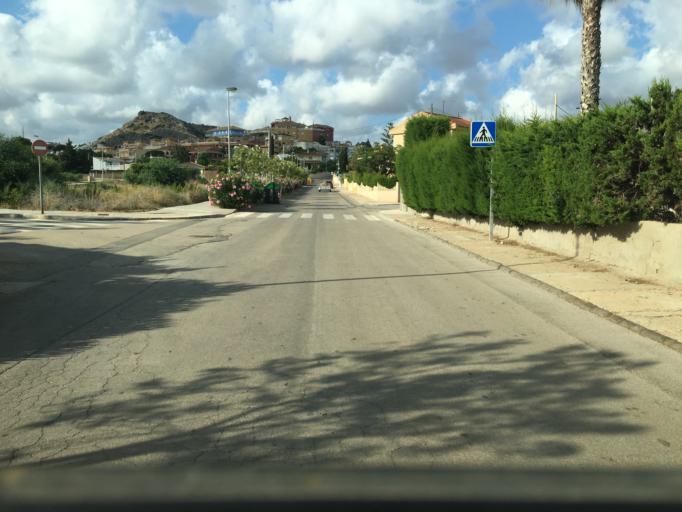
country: ES
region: Murcia
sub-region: Murcia
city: Los Alcazares
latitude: 37.6952
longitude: -0.8424
